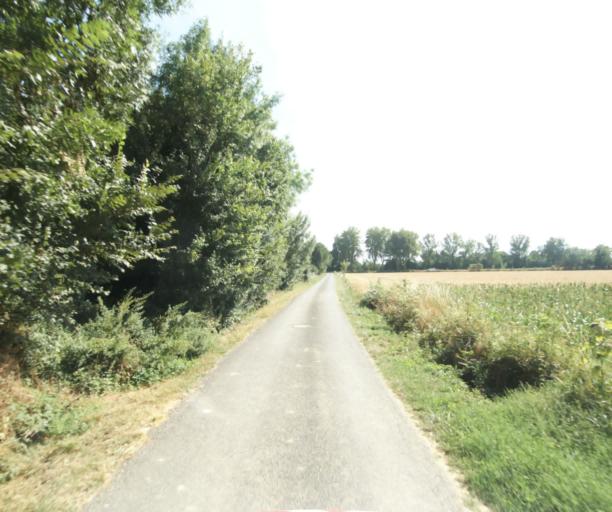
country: FR
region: Midi-Pyrenees
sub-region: Departement de la Haute-Garonne
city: Revel
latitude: 43.4987
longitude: 1.9666
